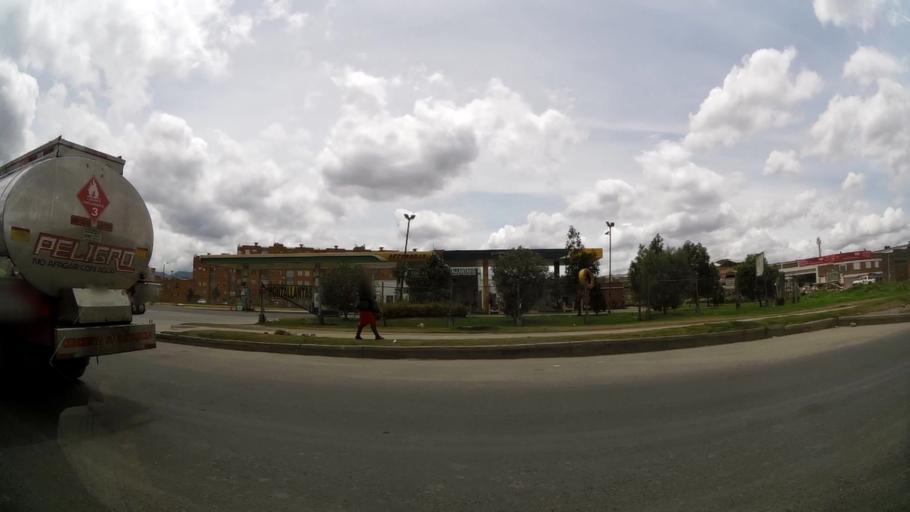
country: CO
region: Bogota D.C.
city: Bogota
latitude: 4.6536
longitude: -74.1424
